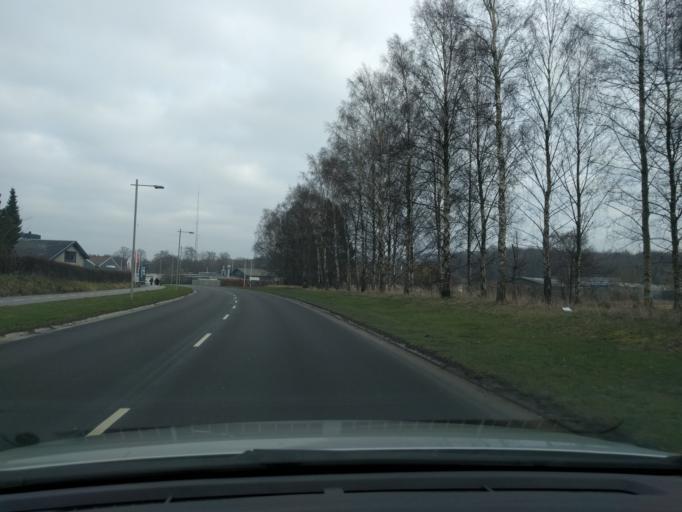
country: DK
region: Zealand
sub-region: Guldborgsund Kommune
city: Nykobing Falster
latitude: 54.7486
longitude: 11.8870
